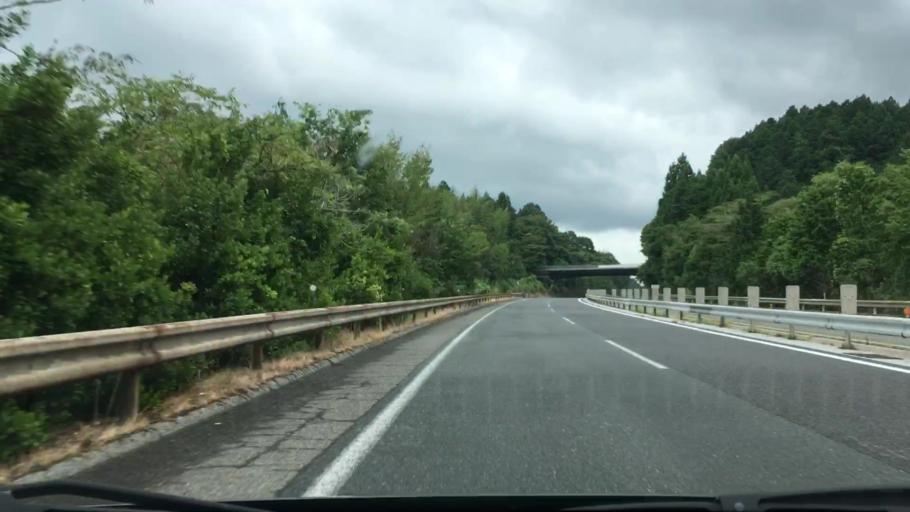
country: JP
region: Okayama
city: Niimi
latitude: 34.9281
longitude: 133.3261
